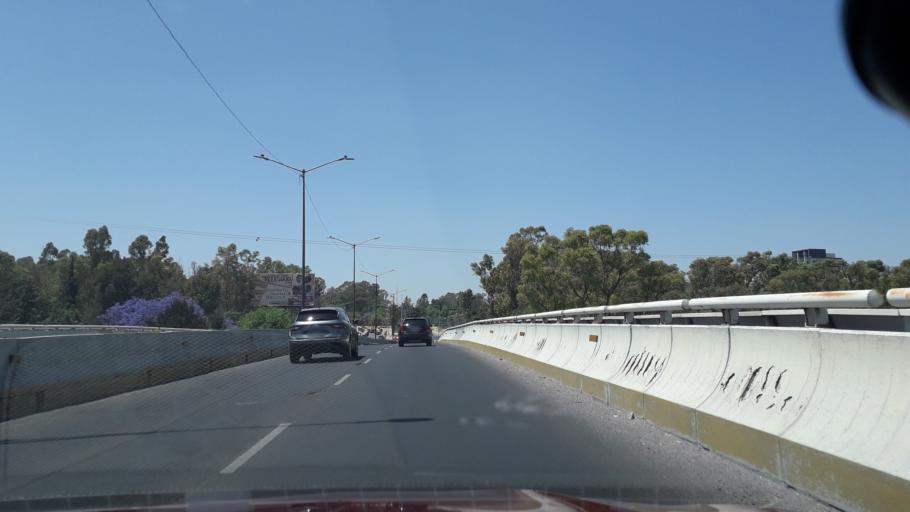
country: MX
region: Puebla
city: Puebla
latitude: 19.0621
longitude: -98.1821
